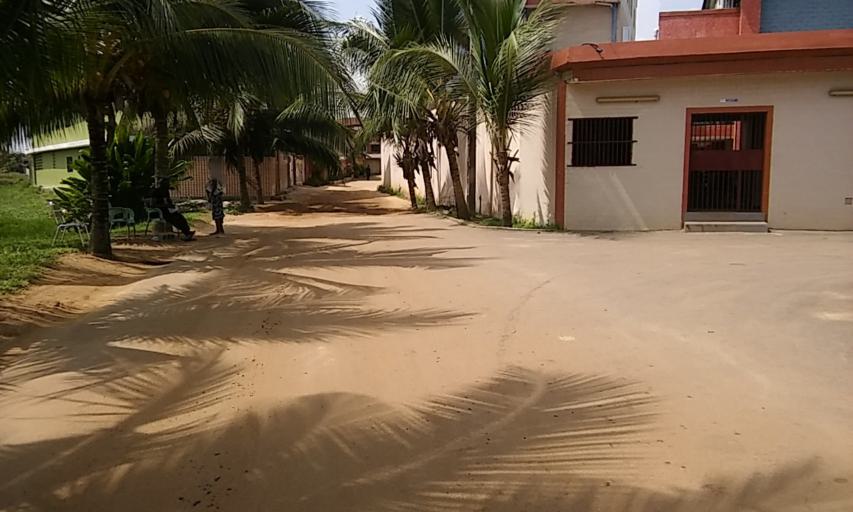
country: CI
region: Sud-Comoe
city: Grand-Bassam
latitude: 5.2178
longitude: -3.7422
